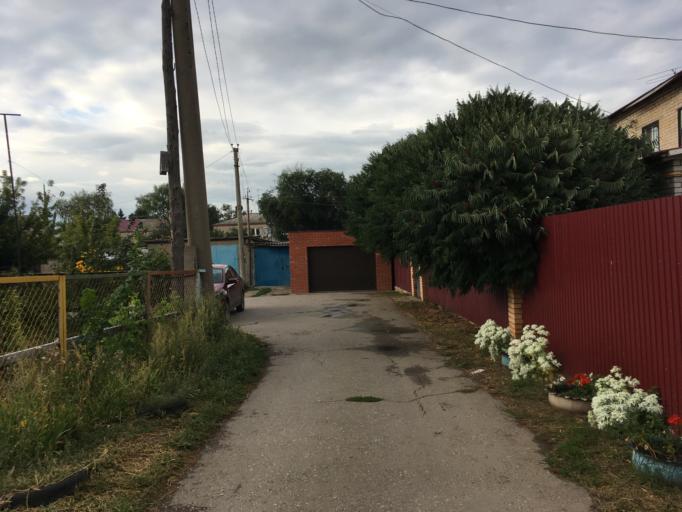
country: RU
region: Samara
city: Bezenchuk
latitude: 52.9868
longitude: 49.4435
